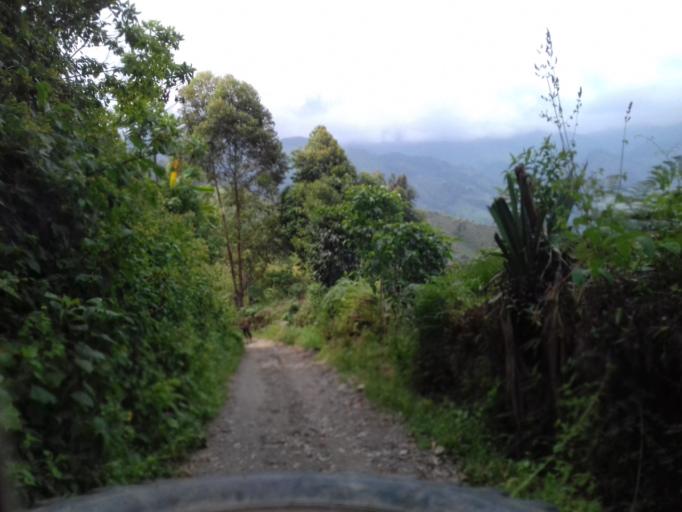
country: CO
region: Tolima
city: Libano
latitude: 4.9293
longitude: -75.0840
